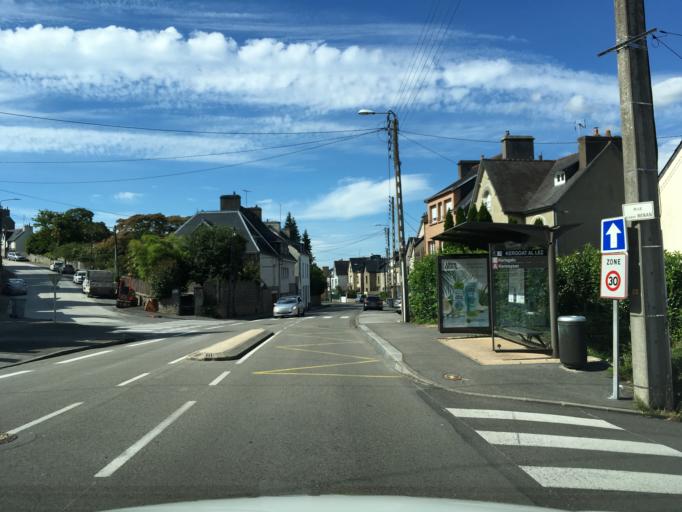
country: FR
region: Brittany
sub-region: Departement du Finistere
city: Quimper
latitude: 47.9905
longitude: -4.0830
